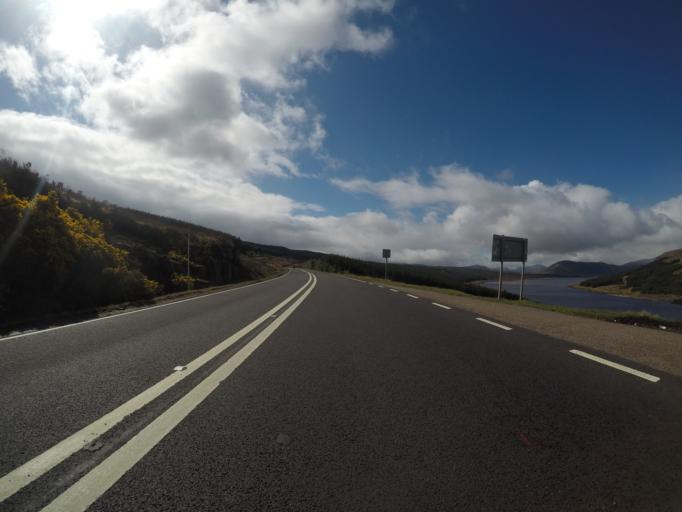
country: GB
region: Scotland
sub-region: Highland
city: Spean Bridge
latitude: 57.1150
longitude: -4.9833
